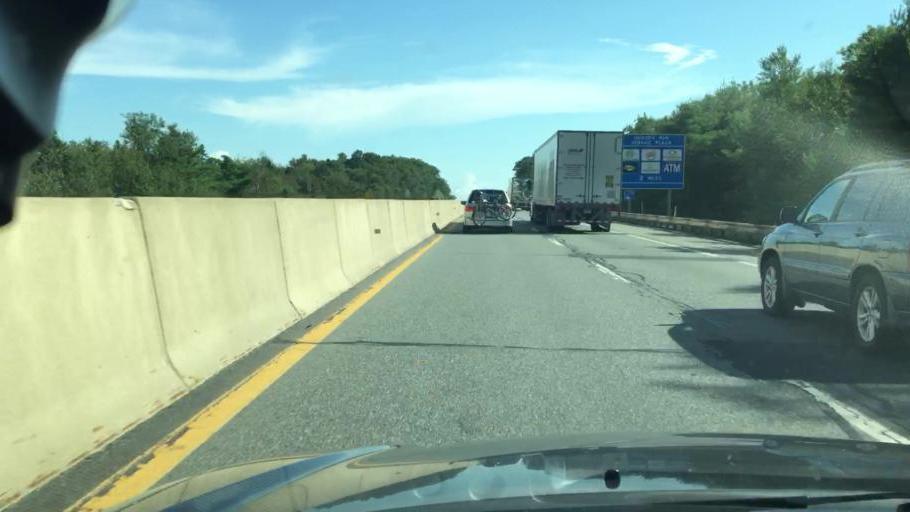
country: US
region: Pennsylvania
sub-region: Carbon County
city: Towamensing Trails
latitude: 40.9925
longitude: -75.6320
